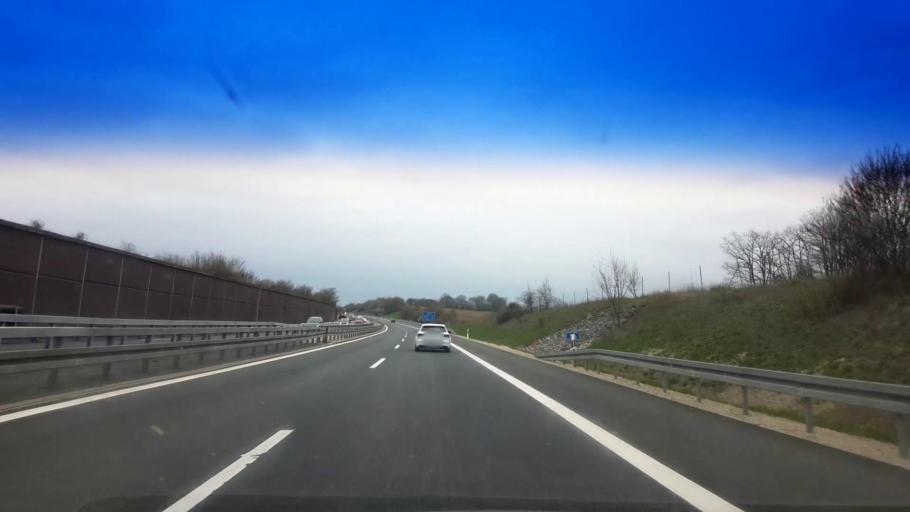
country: DE
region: Bavaria
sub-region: Upper Franconia
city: Schesslitz
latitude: 49.9811
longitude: 11.0369
